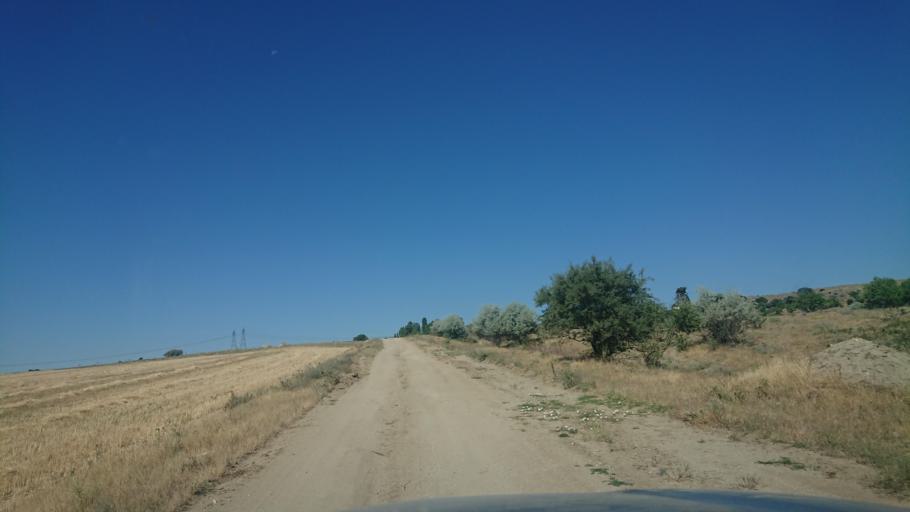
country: TR
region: Aksaray
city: Sariyahsi
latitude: 38.9439
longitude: 33.8781
